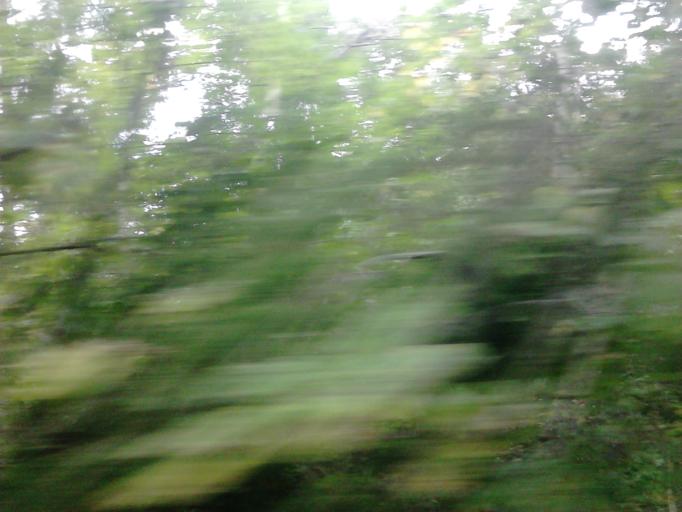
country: PL
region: Lesser Poland Voivodeship
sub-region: Powiat limanowski
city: Limanowa
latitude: 49.7185
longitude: 20.4657
